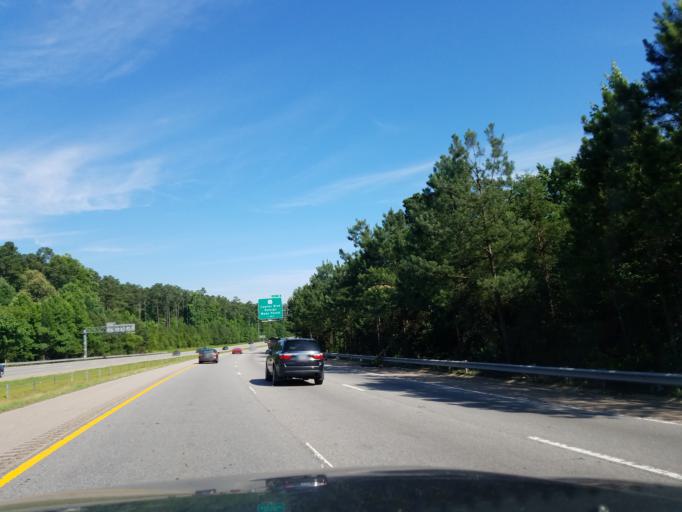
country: US
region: North Carolina
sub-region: Wake County
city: Wake Forest
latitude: 35.8919
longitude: -78.5963
